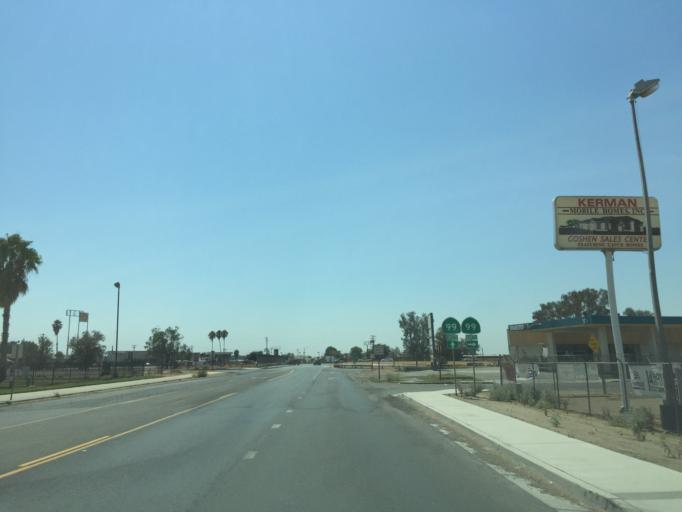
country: US
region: California
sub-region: Tulare County
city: Goshen
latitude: 36.3511
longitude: -119.4254
